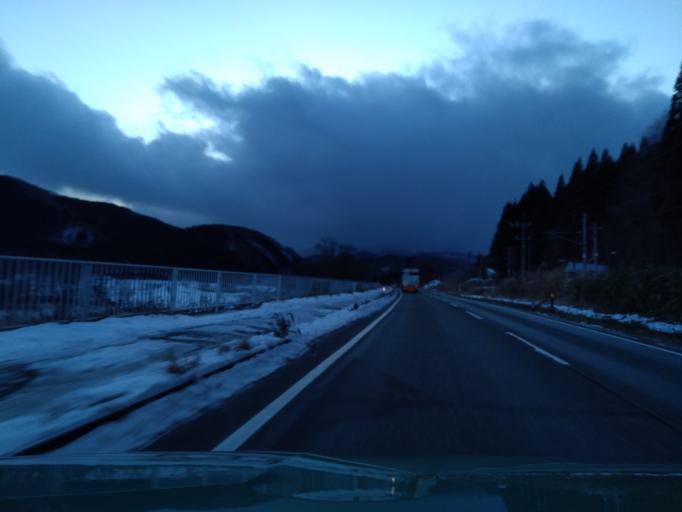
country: JP
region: Iwate
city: Shizukuishi
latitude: 39.6876
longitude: 140.9166
